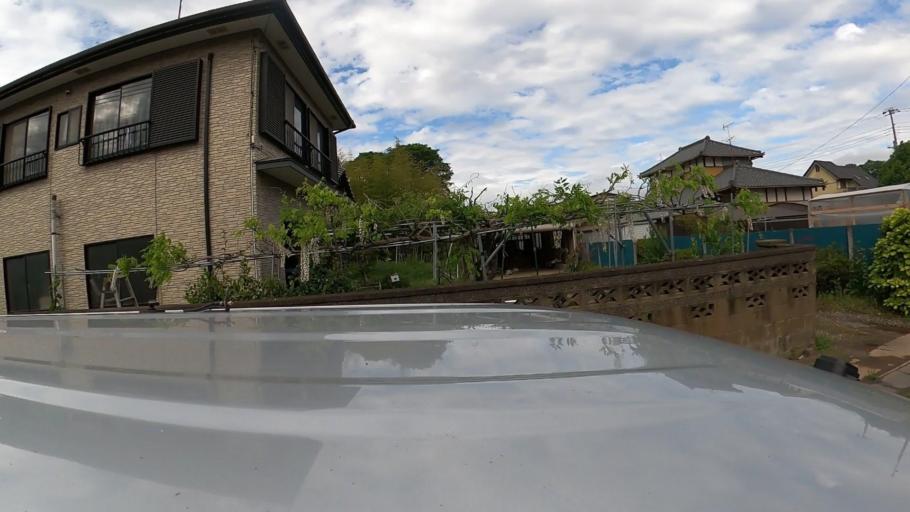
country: JP
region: Ibaraki
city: Ushiku
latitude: 35.9799
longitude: 140.1721
